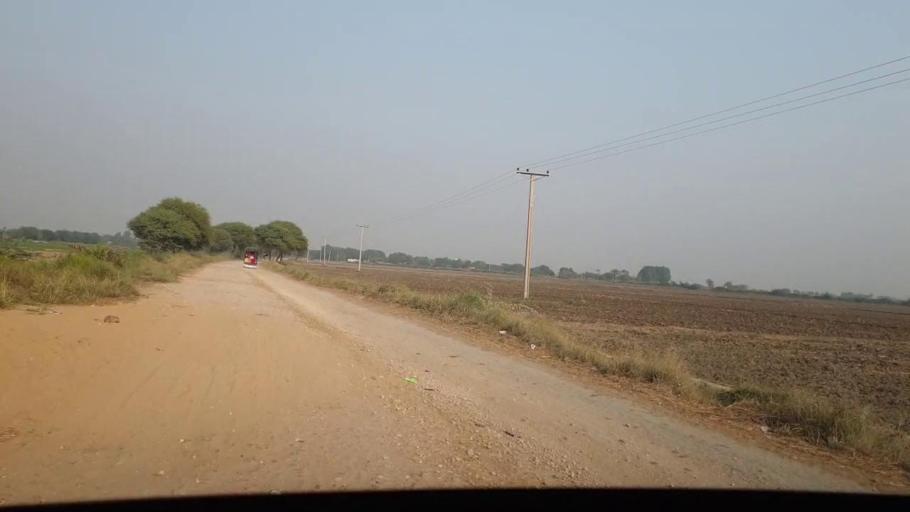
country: PK
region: Sindh
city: Chuhar Jamali
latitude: 24.2506
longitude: 68.0977
